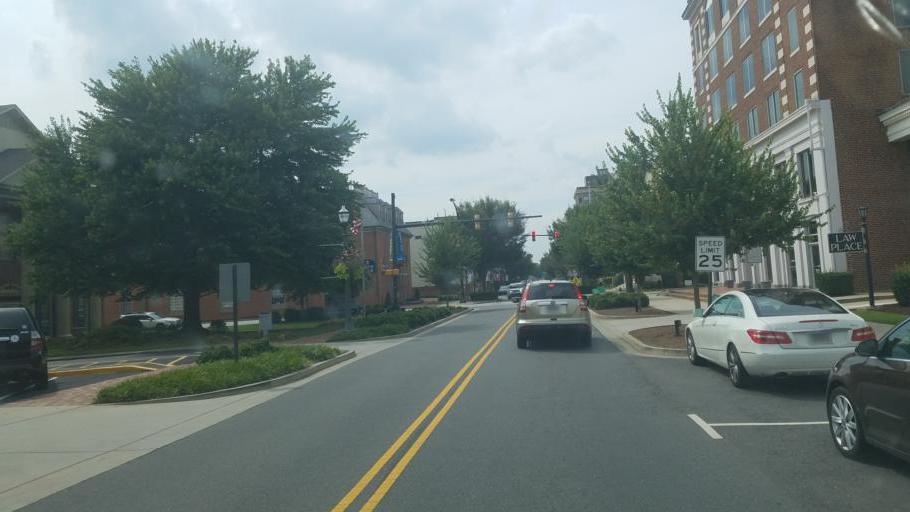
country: US
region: South Carolina
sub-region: York County
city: Rock Hill
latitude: 34.9242
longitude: -81.0249
